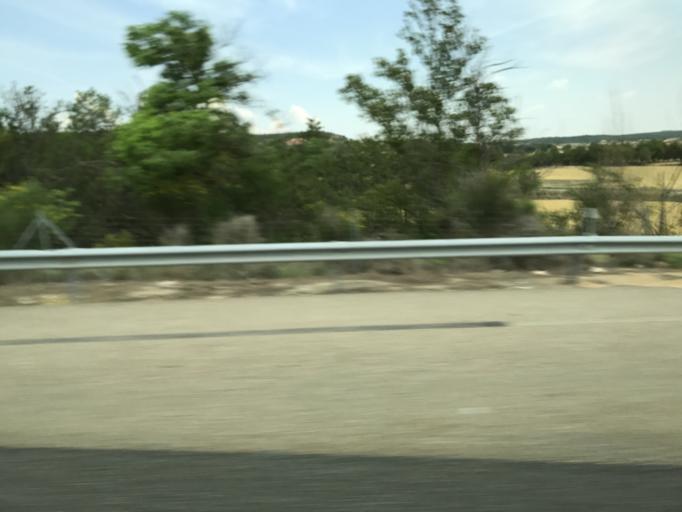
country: ES
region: Castille and Leon
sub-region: Provincia de Burgos
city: Oquillas
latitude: 41.8367
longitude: -3.7086
